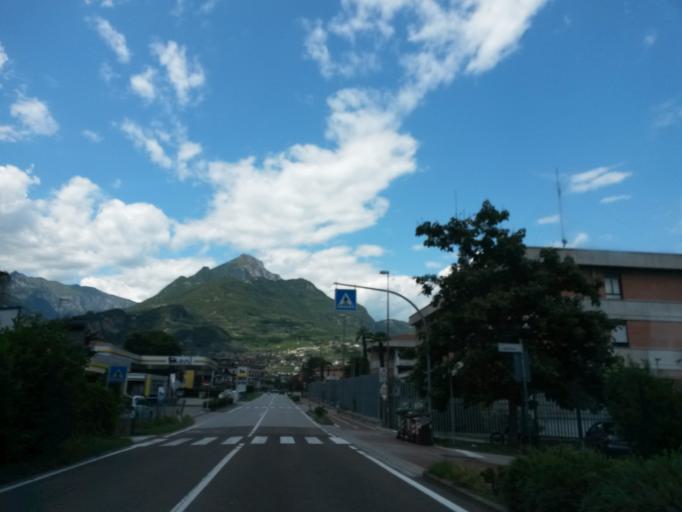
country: IT
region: Trentino-Alto Adige
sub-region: Provincia di Trento
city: Riva del Garda
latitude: 45.8958
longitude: 10.8441
